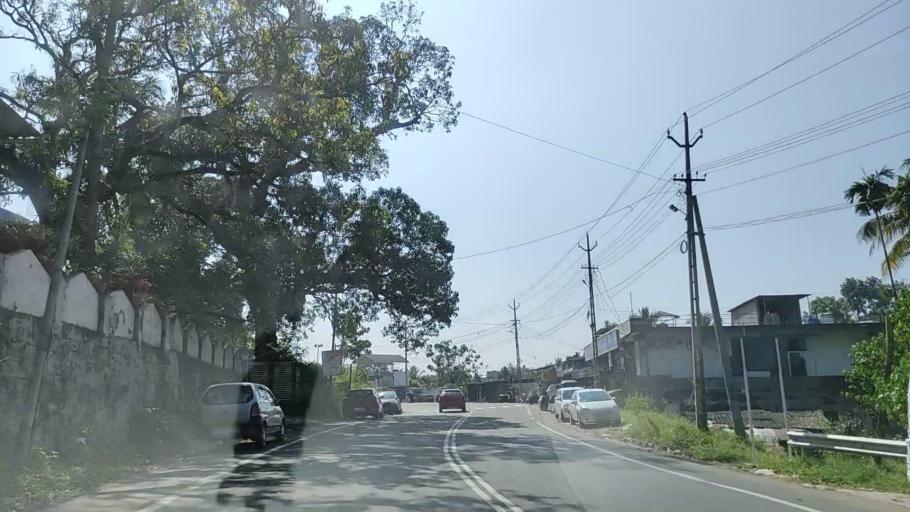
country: IN
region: Kerala
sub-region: Kollam
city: Punalur
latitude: 8.9081
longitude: 77.0533
